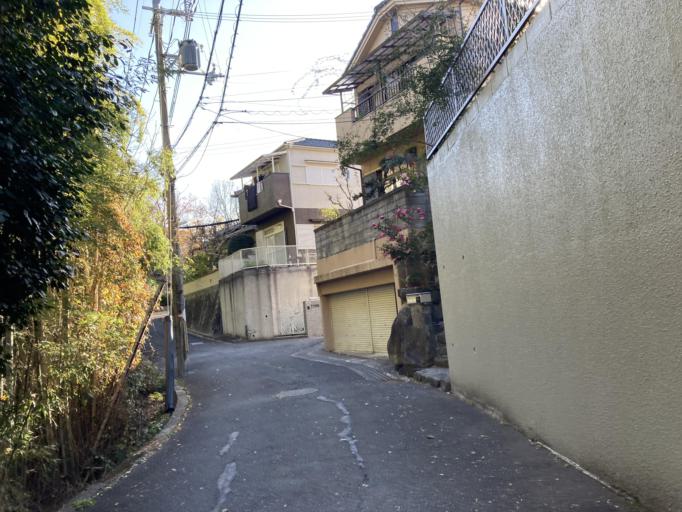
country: JP
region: Nara
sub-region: Ikoma-shi
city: Ikoma
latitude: 34.6825
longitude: 135.7099
